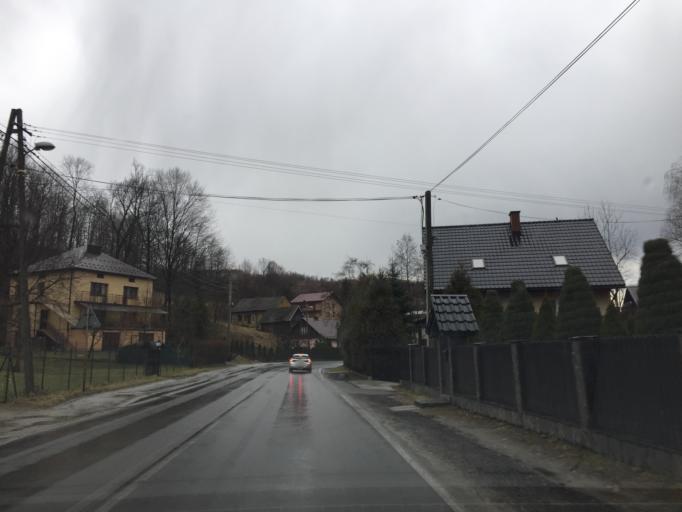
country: PL
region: Lesser Poland Voivodeship
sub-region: Powiat myslenicki
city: Harbutowice
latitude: 49.8172
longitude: 19.7829
